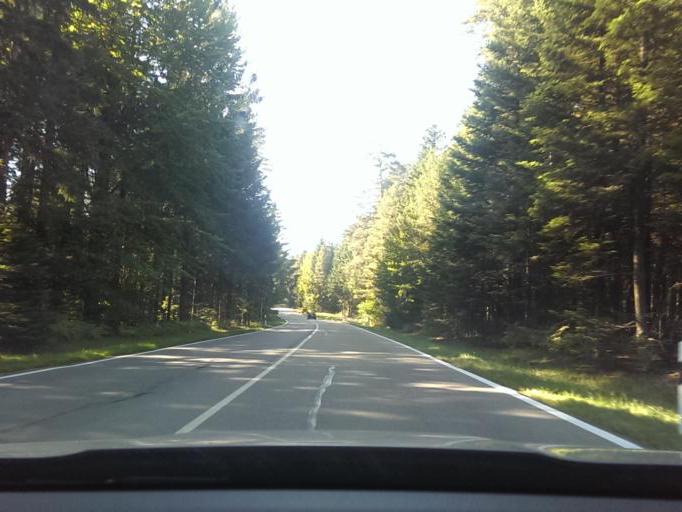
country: DE
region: Baden-Wuerttemberg
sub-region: Karlsruhe Region
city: Simmersfeld
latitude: 48.6392
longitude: 8.4972
